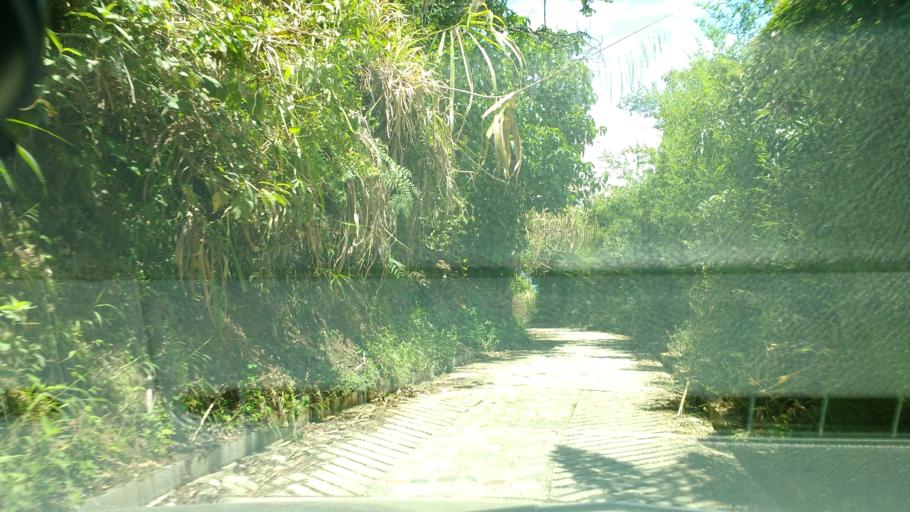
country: CO
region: Antioquia
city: Santa Barbara
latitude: 5.8594
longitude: -75.5582
